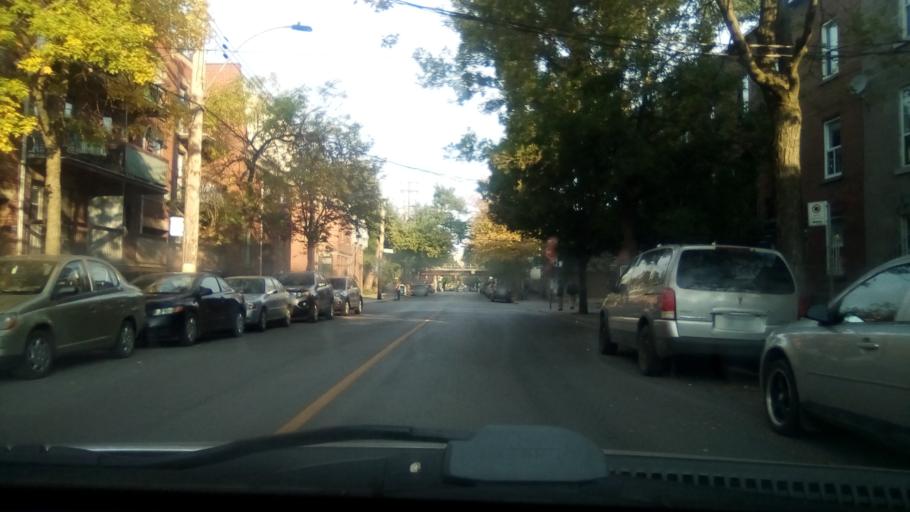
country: CA
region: Quebec
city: Westmount
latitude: 45.4759
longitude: -73.5647
